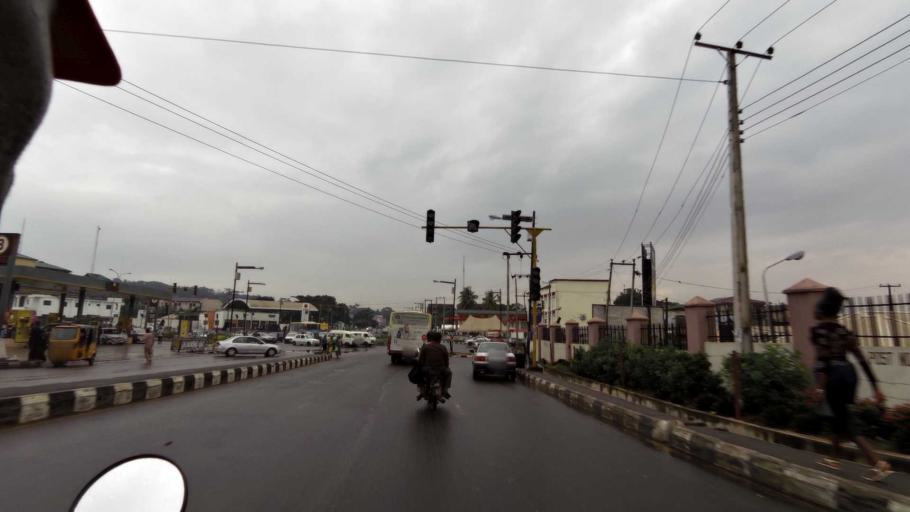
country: NG
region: Oyo
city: Ibadan
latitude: 7.3984
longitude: 3.9084
